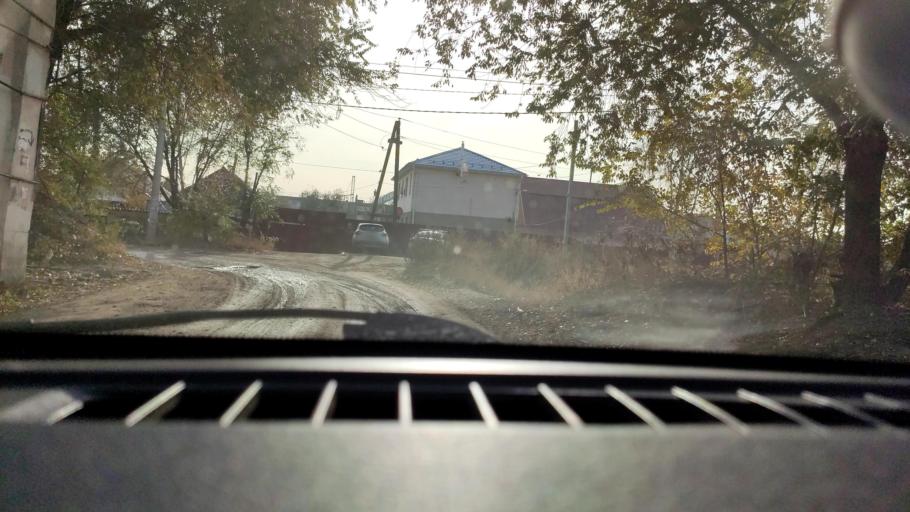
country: RU
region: Samara
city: Samara
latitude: 53.1761
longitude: 50.1905
